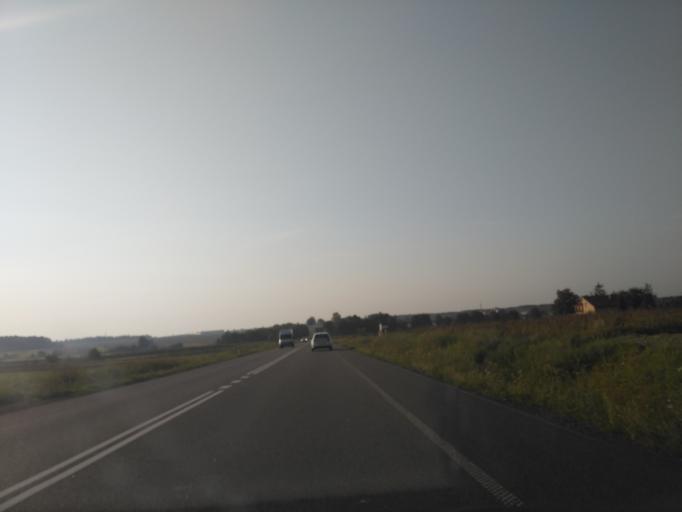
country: PL
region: Lublin Voivodeship
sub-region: Powiat janowski
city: Modliborzyce
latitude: 50.7367
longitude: 22.3522
